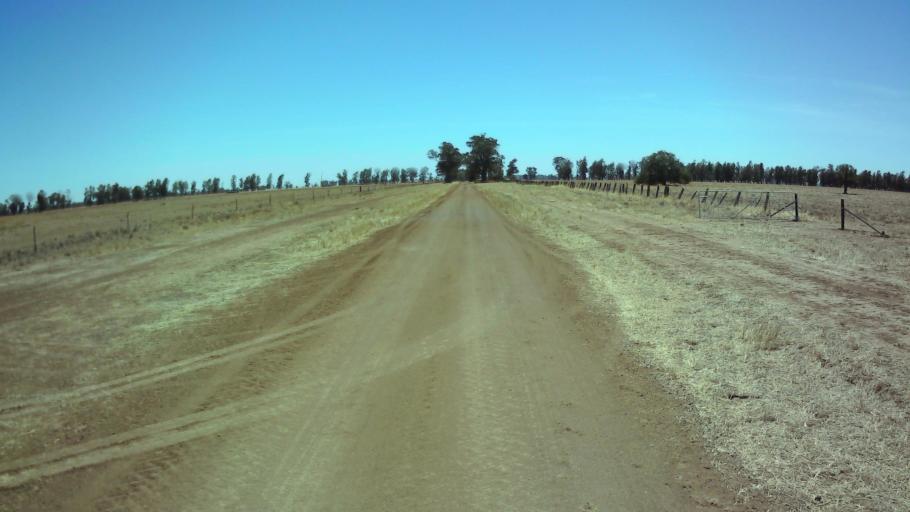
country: AU
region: New South Wales
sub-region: Weddin
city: Grenfell
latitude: -33.9743
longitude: 147.7374
